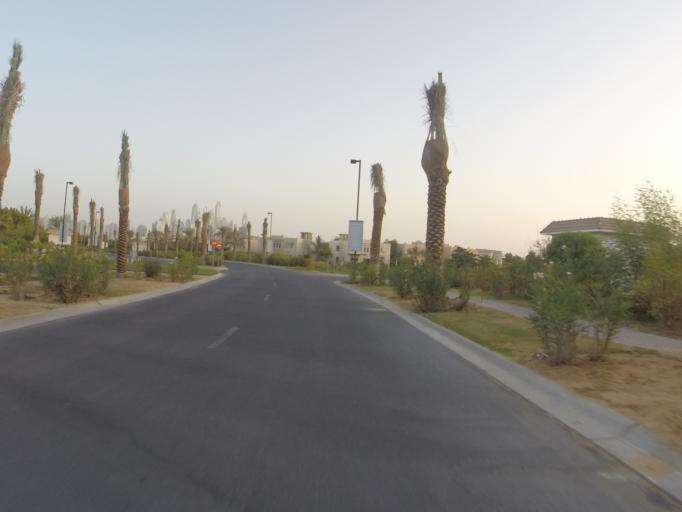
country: AE
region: Dubai
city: Dubai
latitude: 25.0565
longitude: 55.1599
